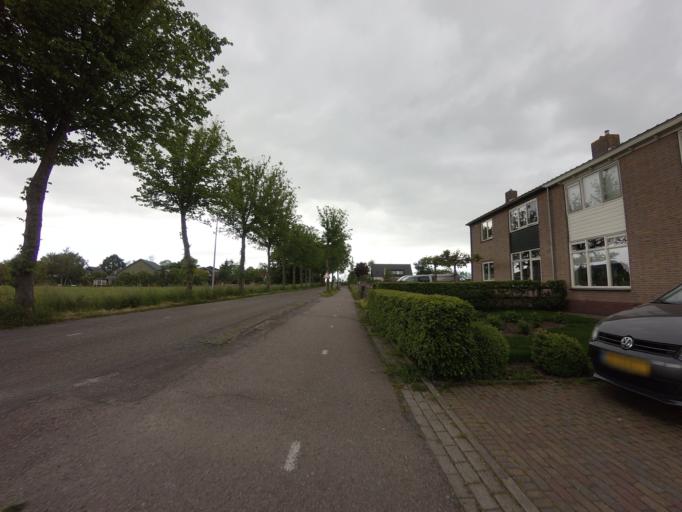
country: NL
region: North Holland
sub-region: Gemeente Hoorn
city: Hoorn
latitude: 52.6523
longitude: 5.0042
